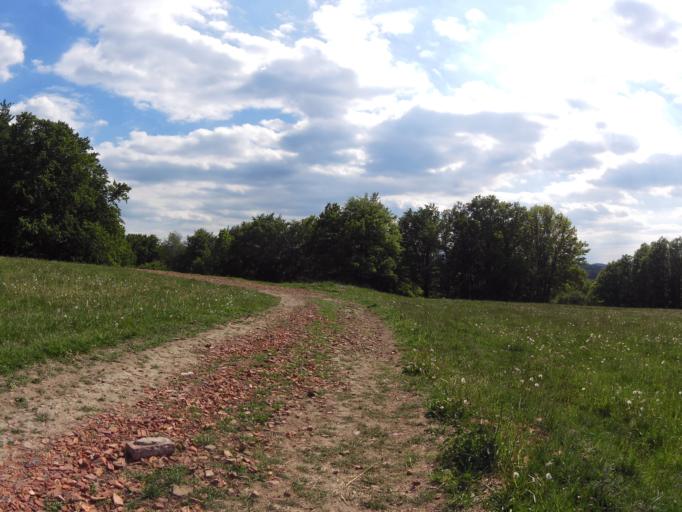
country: DE
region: Thuringia
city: Seebach
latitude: 50.9550
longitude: 10.4284
